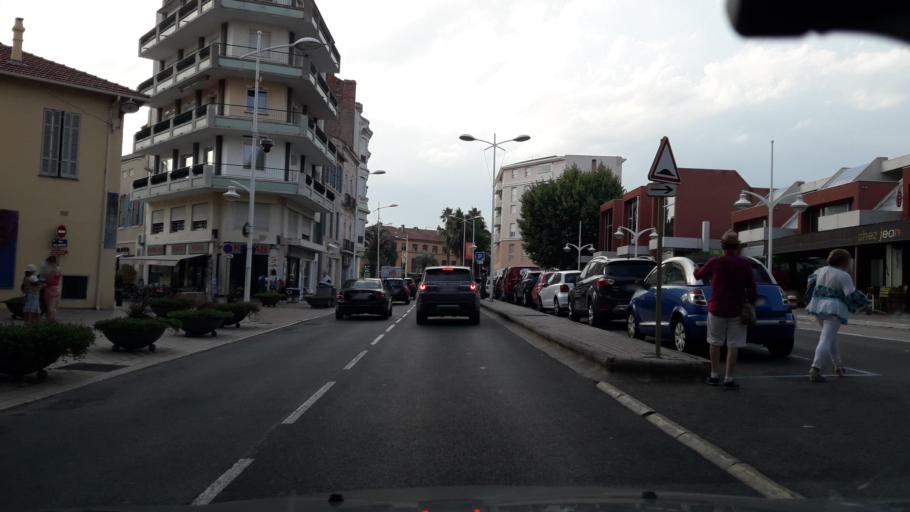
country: FR
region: Provence-Alpes-Cote d'Azur
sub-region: Departement du Var
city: Saint-Raphael
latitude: 43.4231
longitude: 6.7692
